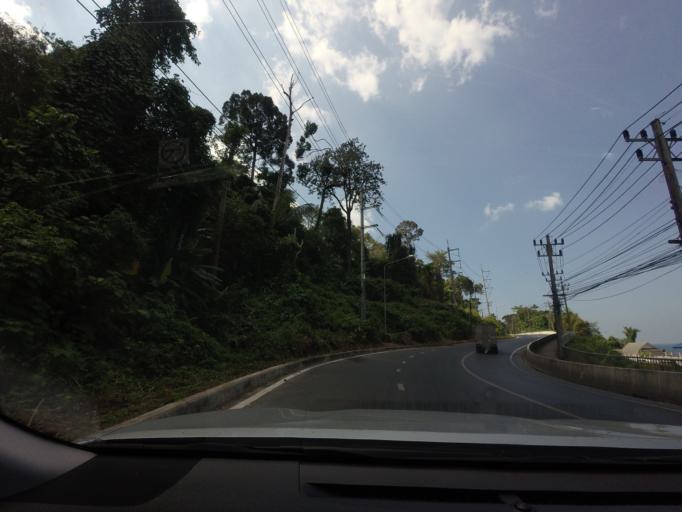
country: TH
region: Phangnga
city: Ban Khao Lak
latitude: 8.6295
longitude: 98.2446
